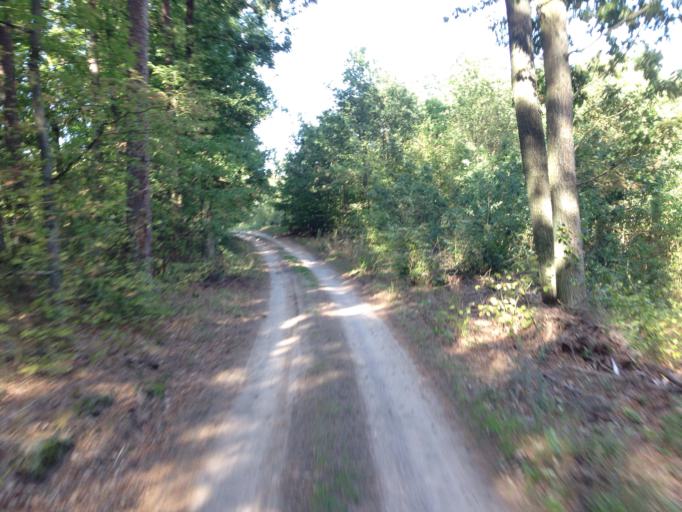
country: PL
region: Warmian-Masurian Voivodeship
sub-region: Powiat dzialdowski
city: Lidzbark
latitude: 53.2249
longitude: 19.7492
